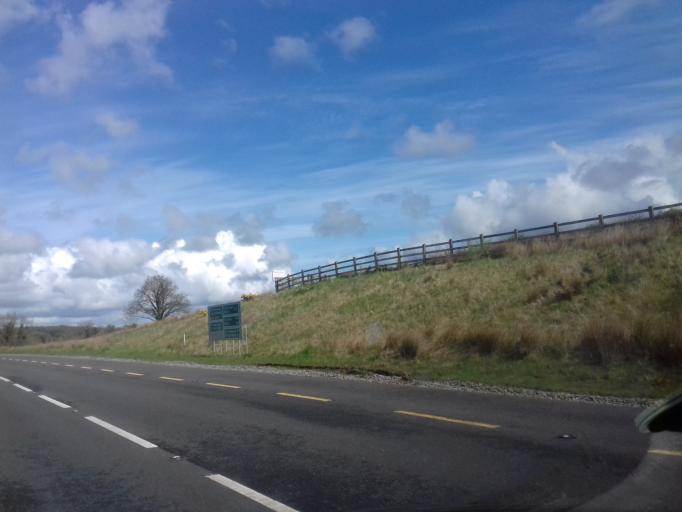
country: IE
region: Ulster
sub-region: An Cabhan
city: Belturbet
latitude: 54.0818
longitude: -7.4341
